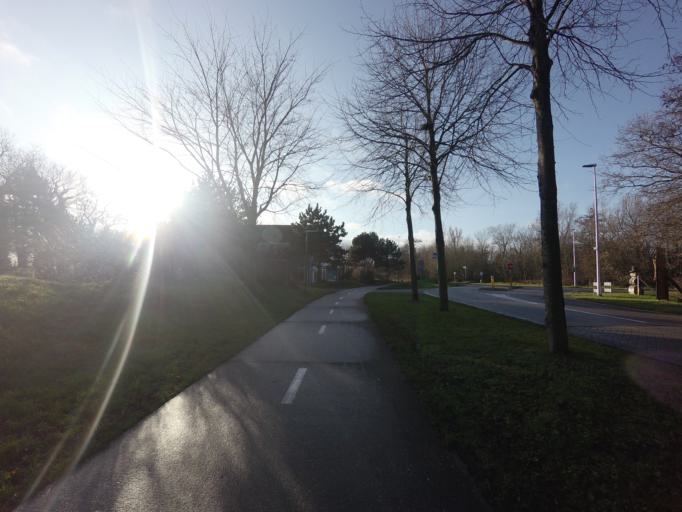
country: NL
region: North Holland
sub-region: Gemeente Texel
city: Den Burg
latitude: 53.1516
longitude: 4.8661
